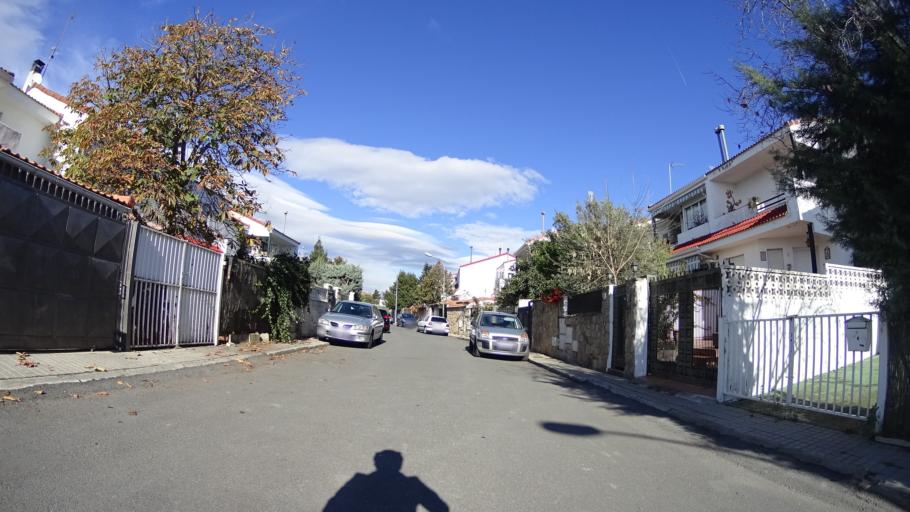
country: ES
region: Madrid
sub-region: Provincia de Madrid
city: Galapagar
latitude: 40.5767
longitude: -4.0137
